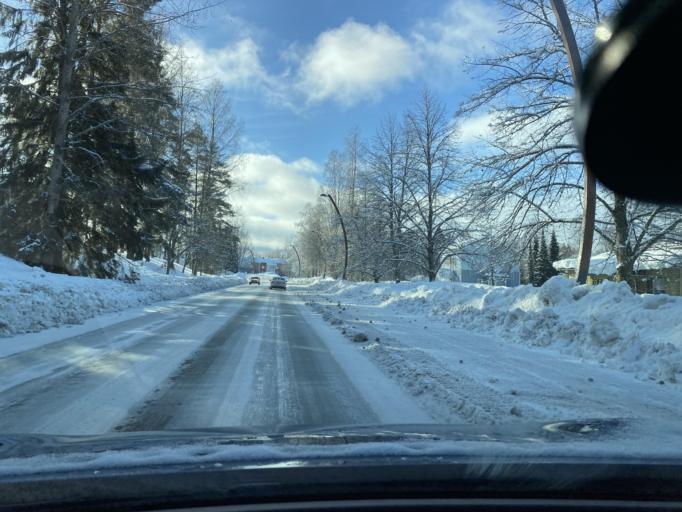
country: FI
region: Southern Savonia
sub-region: Mikkeli
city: Kangasniemi
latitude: 61.9924
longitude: 26.6447
